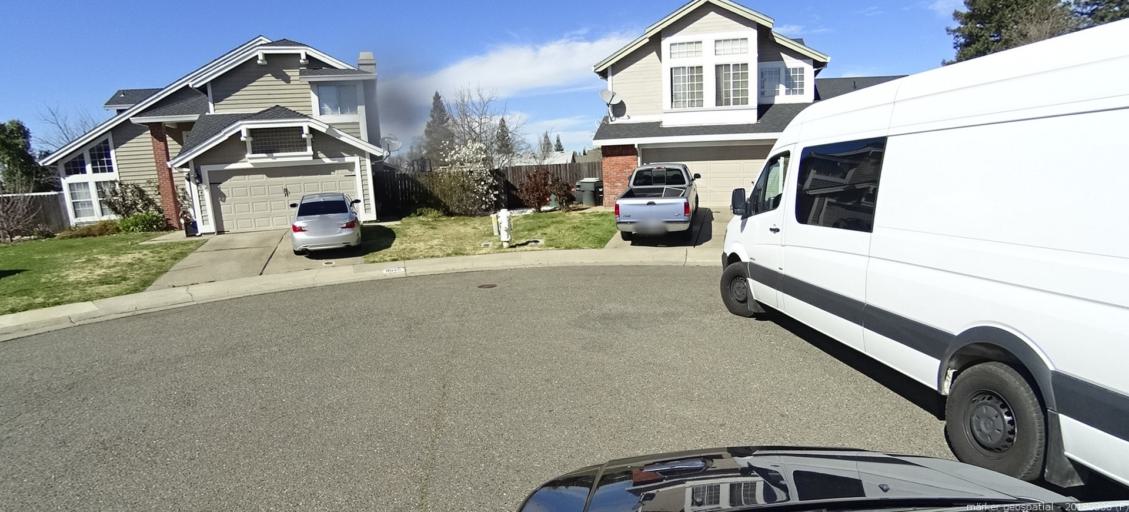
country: US
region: California
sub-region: Sacramento County
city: Vineyard
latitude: 38.4641
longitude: -121.3630
